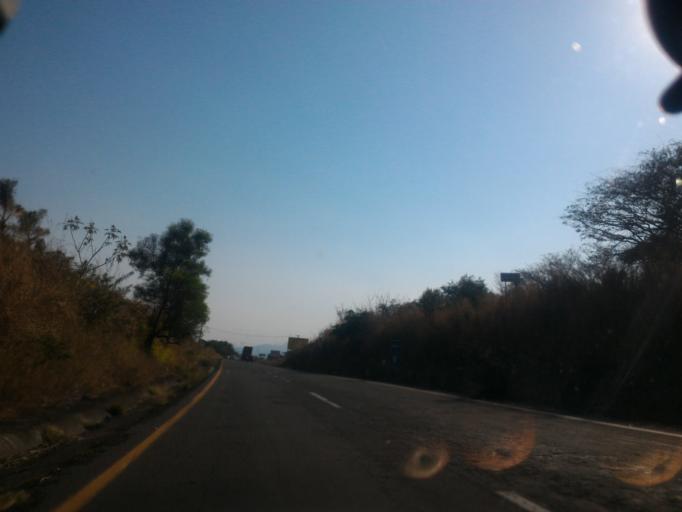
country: MX
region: Colima
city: Colima
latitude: 19.2635
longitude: -103.6821
